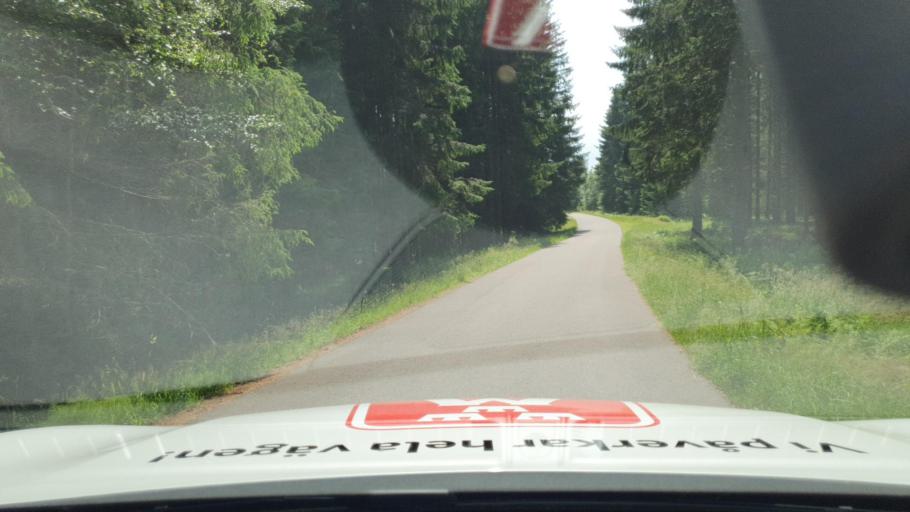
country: SE
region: Vaermland
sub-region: Sunne Kommun
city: Sunne
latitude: 59.9747
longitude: 13.0971
